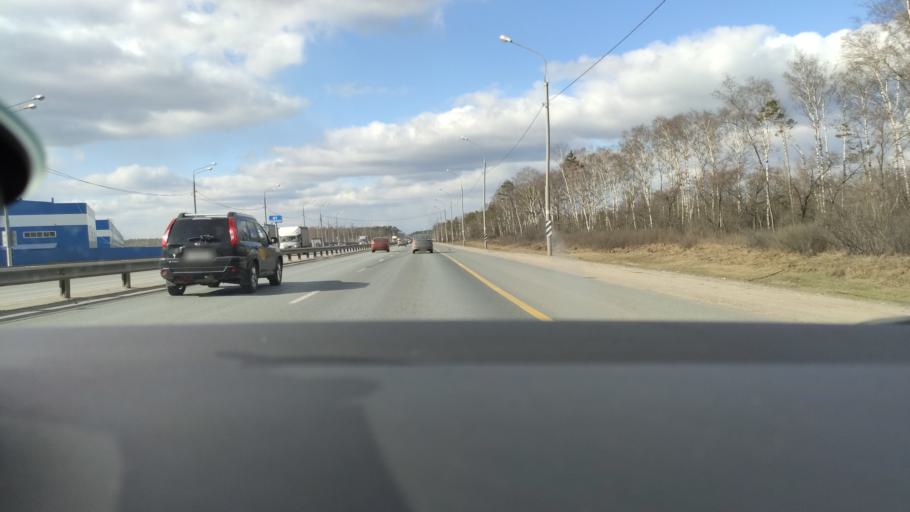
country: RU
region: Moskovskaya
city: Obukhovo
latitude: 55.8268
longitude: 38.2440
